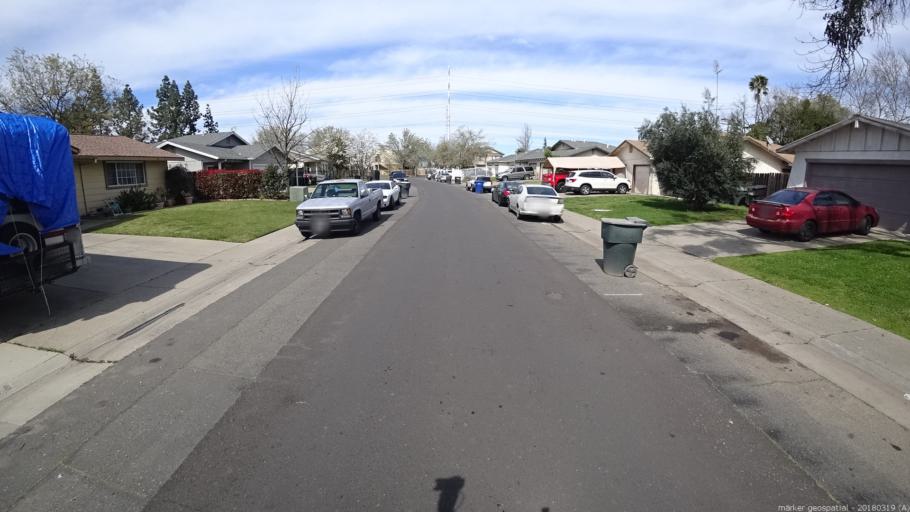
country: US
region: California
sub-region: Sacramento County
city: Parkway
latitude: 38.5073
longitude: -121.4466
